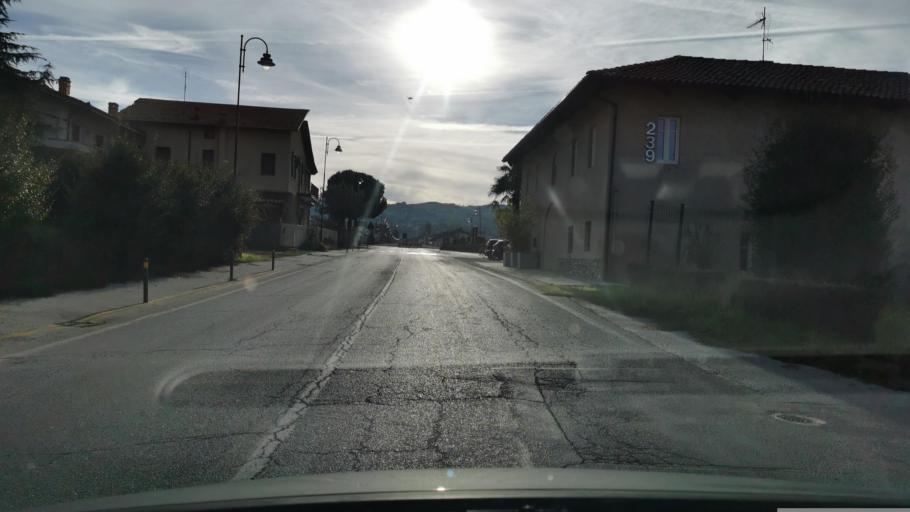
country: IT
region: Piedmont
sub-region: Provincia di Cuneo
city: Dogliani
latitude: 44.5373
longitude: 7.9338
